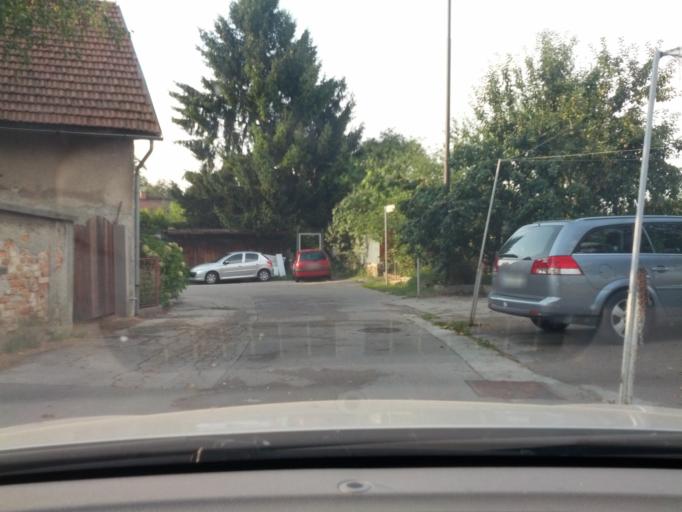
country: SI
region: Ljubljana
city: Ljubljana
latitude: 46.0638
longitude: 14.5002
